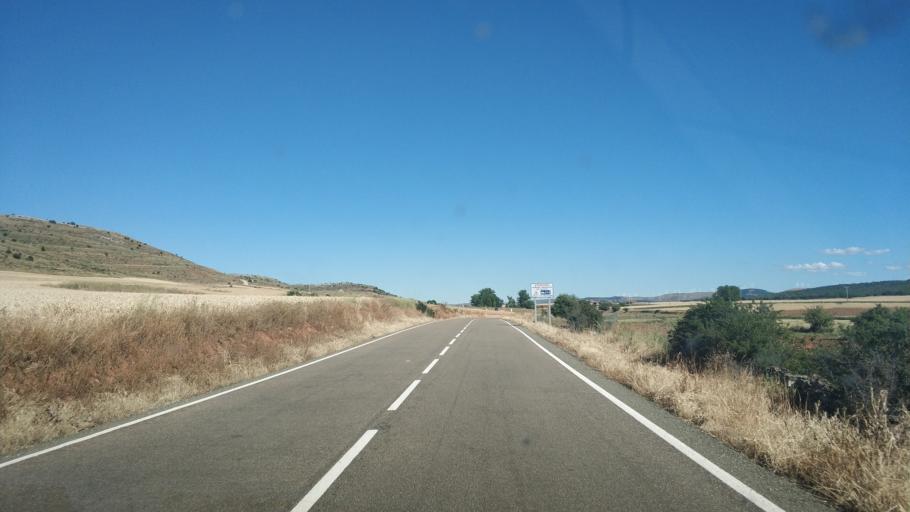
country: ES
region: Castille and Leon
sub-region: Provincia de Soria
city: Montejo de Tiermes
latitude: 41.3654
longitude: -3.1915
